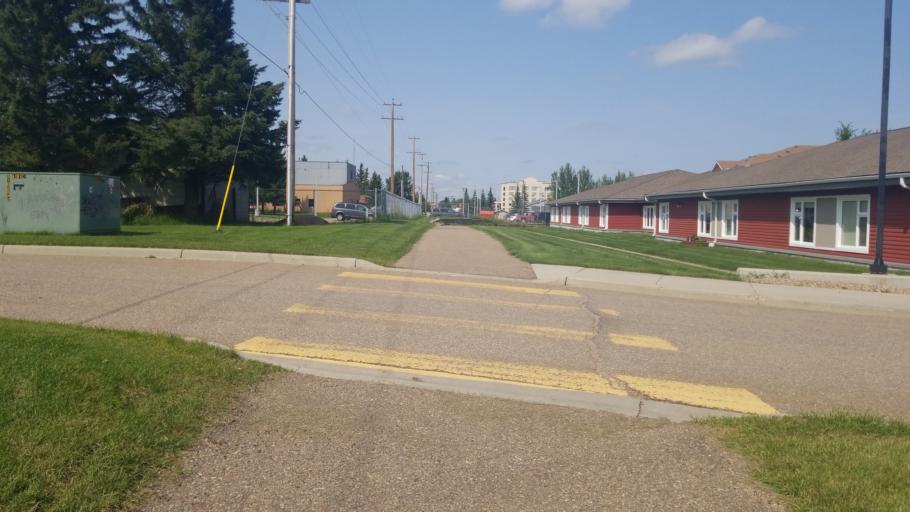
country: CA
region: Saskatchewan
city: Lloydminster
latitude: 53.2733
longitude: -110.0176
